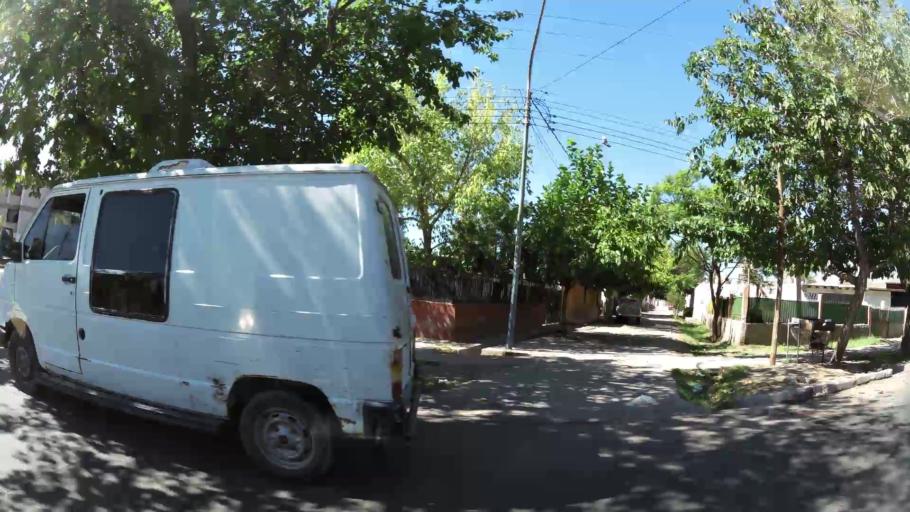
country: AR
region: Mendoza
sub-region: Departamento de Godoy Cruz
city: Godoy Cruz
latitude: -32.9047
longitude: -68.8682
